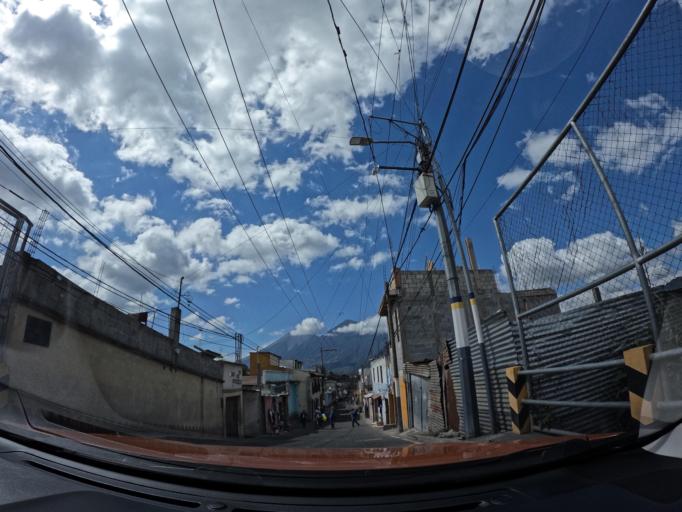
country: GT
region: Sacatepequez
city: Ciudad Vieja
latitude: 14.5256
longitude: -90.7551
